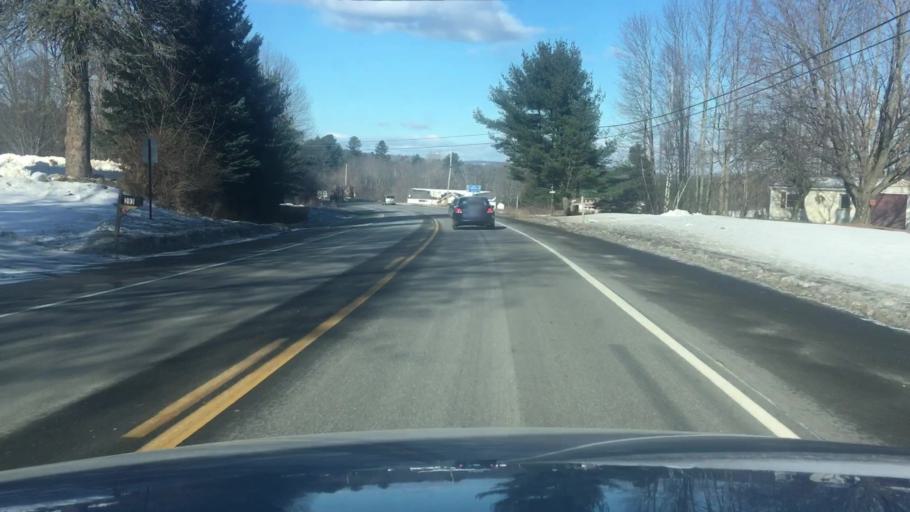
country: US
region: Maine
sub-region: Somerset County
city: Fairfield
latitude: 44.6328
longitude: -69.6795
